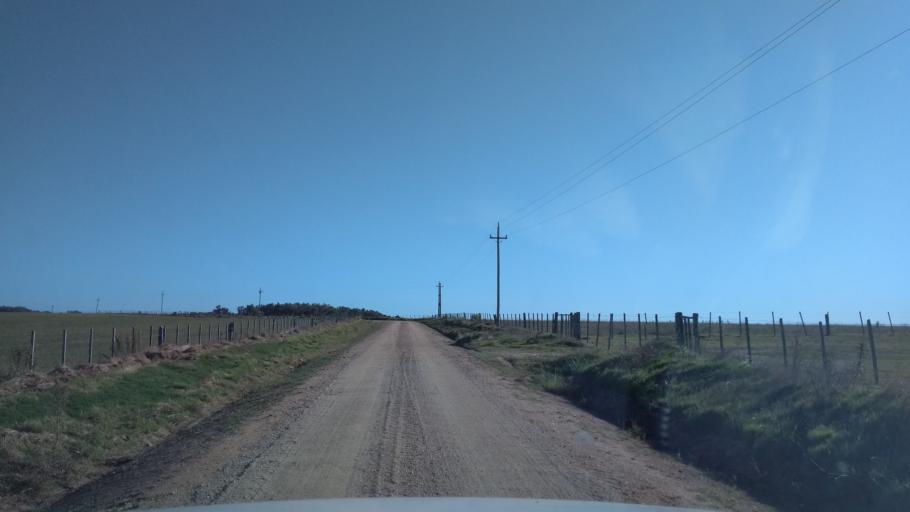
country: UY
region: Florida
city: Casupa
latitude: -34.0363
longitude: -55.7805
